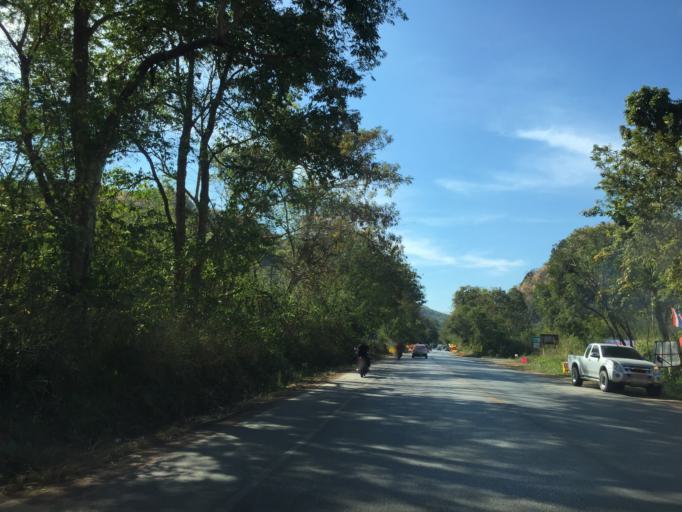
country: TH
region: Loei
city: Wang Saphung
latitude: 17.2883
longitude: 101.8329
